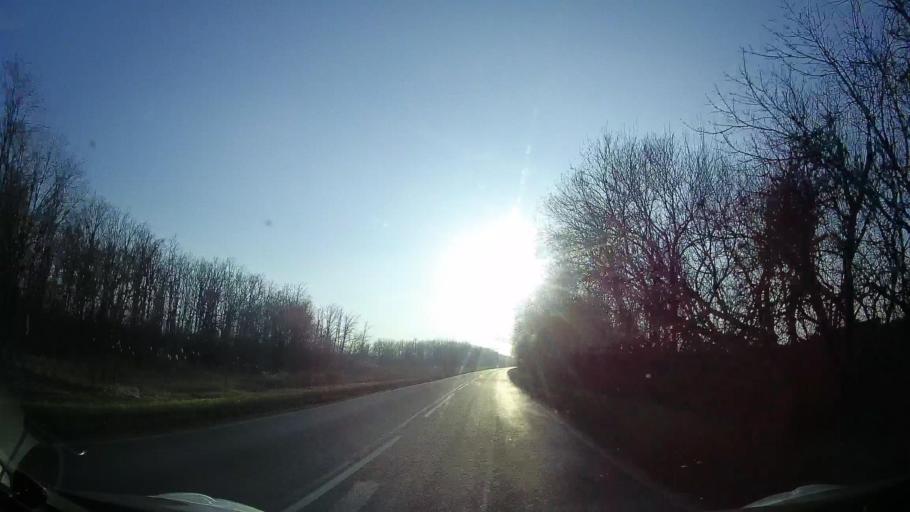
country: RU
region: Rostov
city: Ol'ginskaya
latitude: 47.1636
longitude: 39.9354
